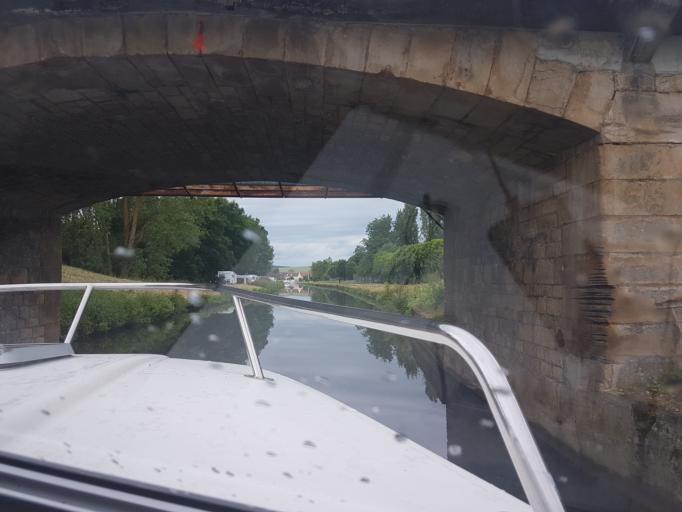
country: FR
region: Bourgogne
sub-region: Departement de l'Yonne
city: Saint-Bris-le-Vineux
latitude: 47.7063
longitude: 3.6363
